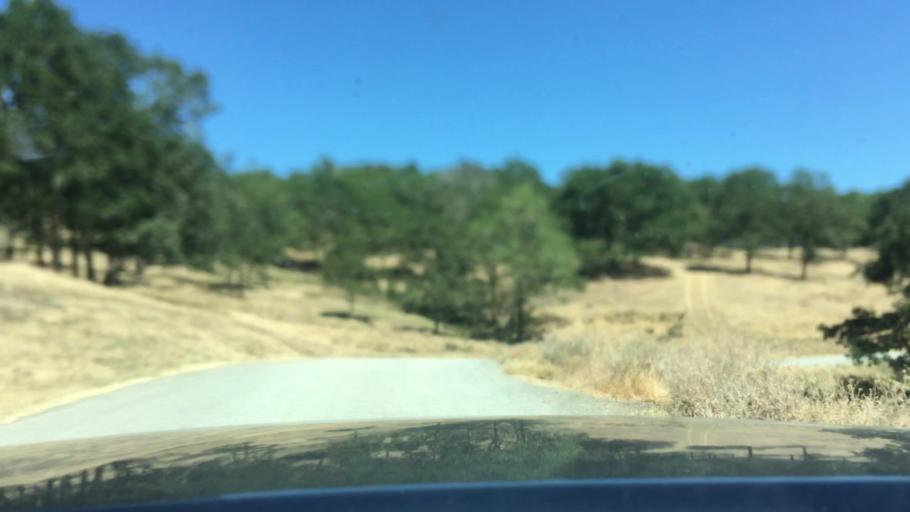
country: US
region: Oregon
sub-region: Douglas County
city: Winston
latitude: 43.1394
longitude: -123.4396
